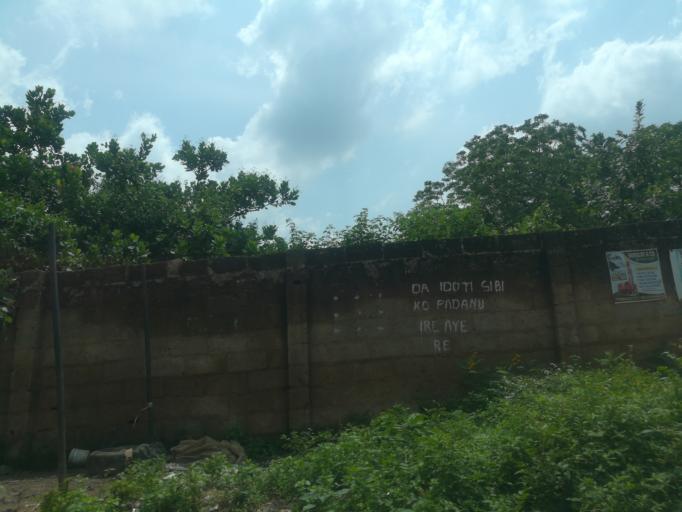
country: NG
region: Oyo
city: Moniya
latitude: 7.4560
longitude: 3.9641
